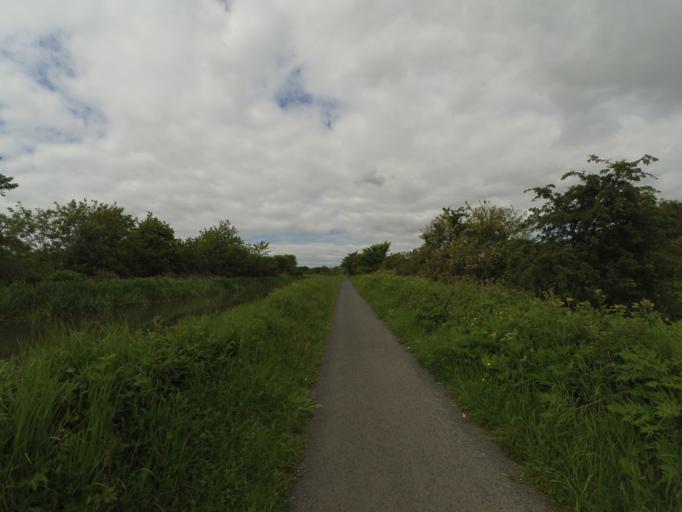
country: GB
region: Scotland
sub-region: Falkirk
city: Polmont
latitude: 55.9773
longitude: -3.6791
